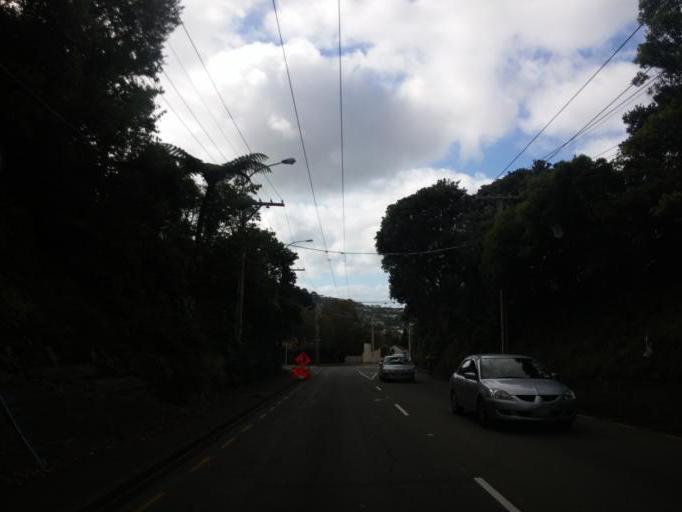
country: NZ
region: Wellington
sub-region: Wellington City
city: Kelburn
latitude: -41.2819
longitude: 174.7472
